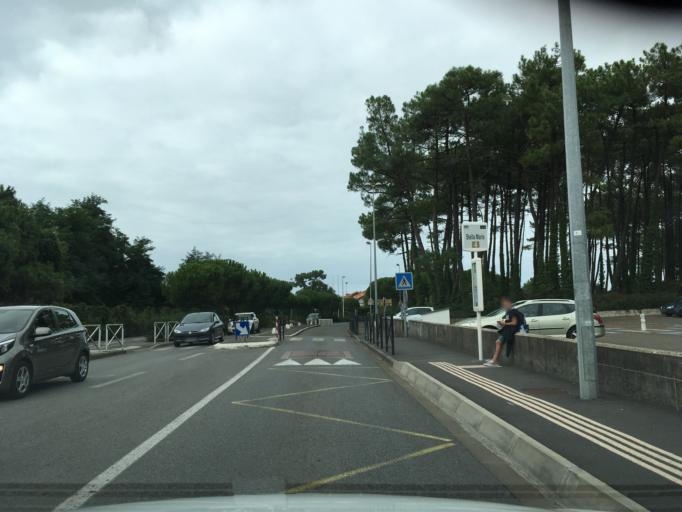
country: FR
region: Aquitaine
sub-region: Departement des Pyrenees-Atlantiques
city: Anglet
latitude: 43.5000
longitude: -1.5277
